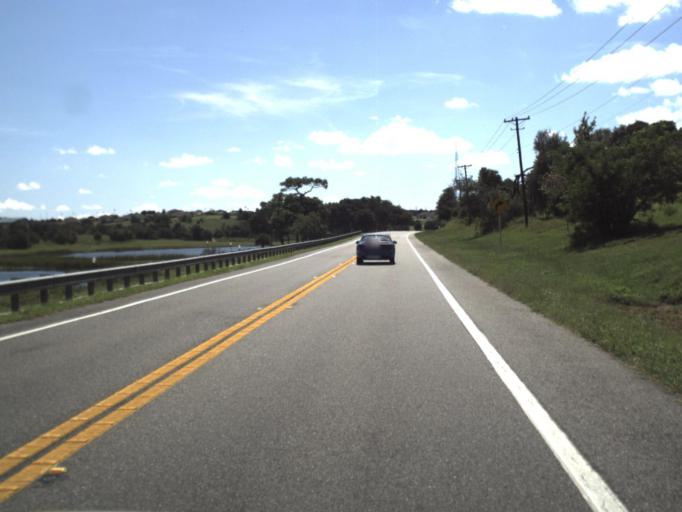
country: US
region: Florida
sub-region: Polk County
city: Dundee
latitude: 28.0209
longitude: -81.6113
